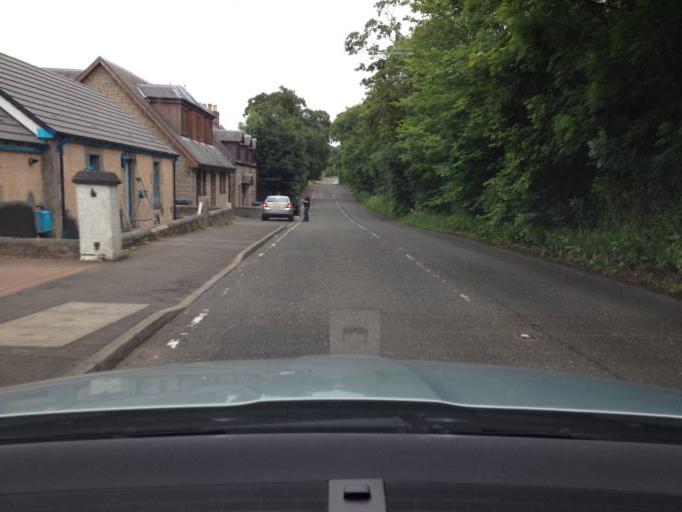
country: GB
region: Scotland
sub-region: West Lothian
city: Mid Calder
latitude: 55.8885
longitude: -3.5006
